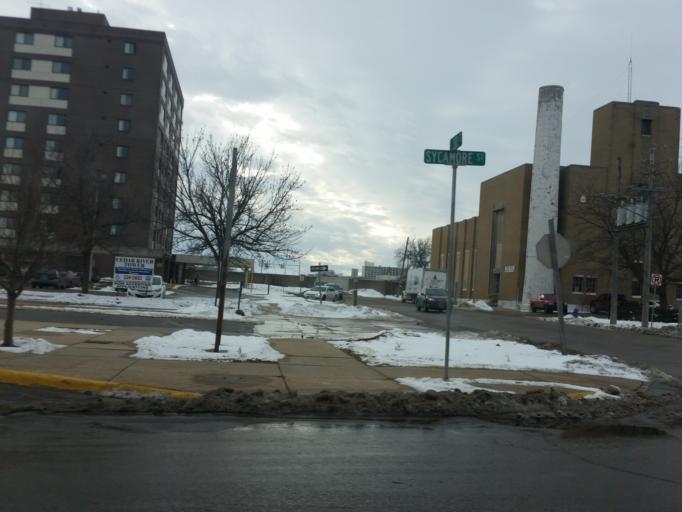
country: US
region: Iowa
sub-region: Black Hawk County
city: Waterloo
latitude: 42.4996
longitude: -92.3380
